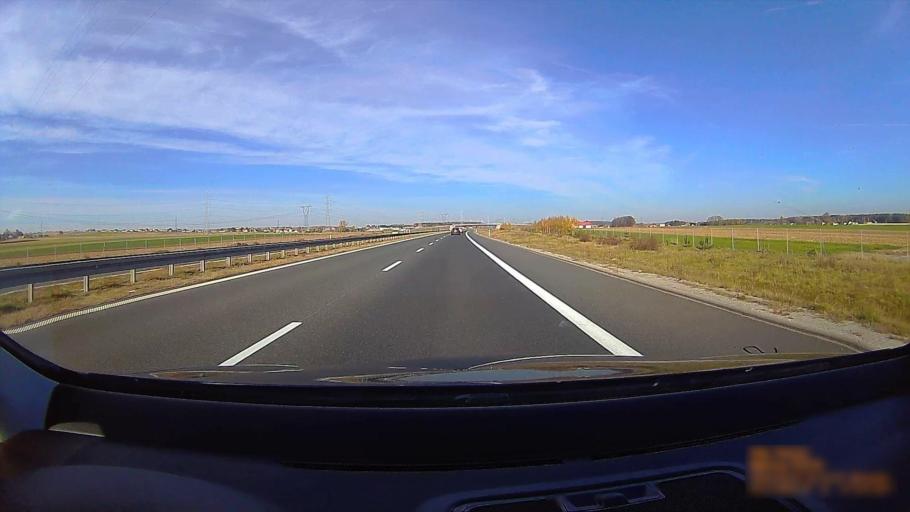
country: PL
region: Greater Poland Voivodeship
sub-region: Powiat ostrowski
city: Przygodzice
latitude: 51.5943
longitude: 17.8498
